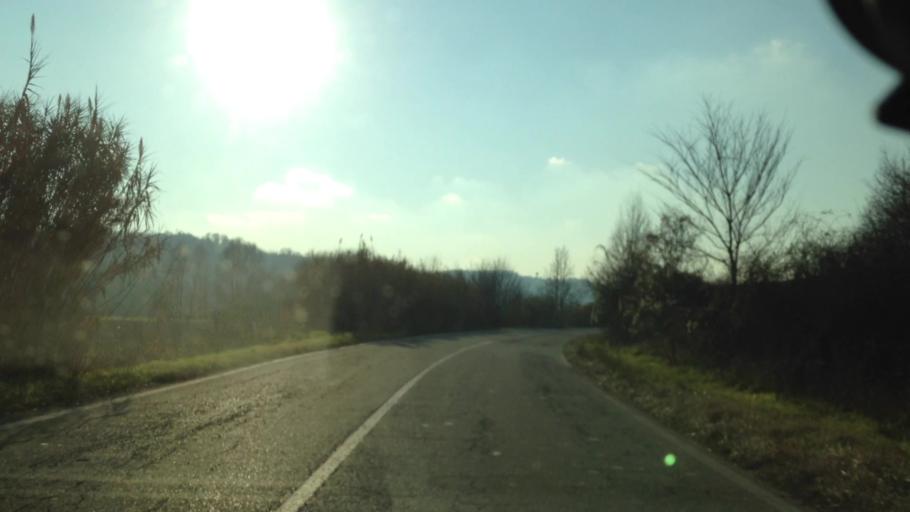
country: IT
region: Piedmont
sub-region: Provincia di Alessandria
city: Masio
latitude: 44.8402
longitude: 8.3893
